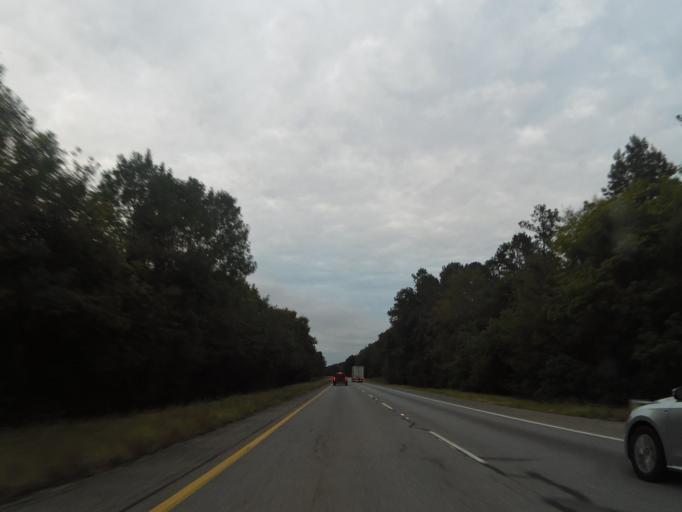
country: US
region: Alabama
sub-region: Saint Clair County
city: Steele
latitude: 33.9007
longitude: -86.2306
